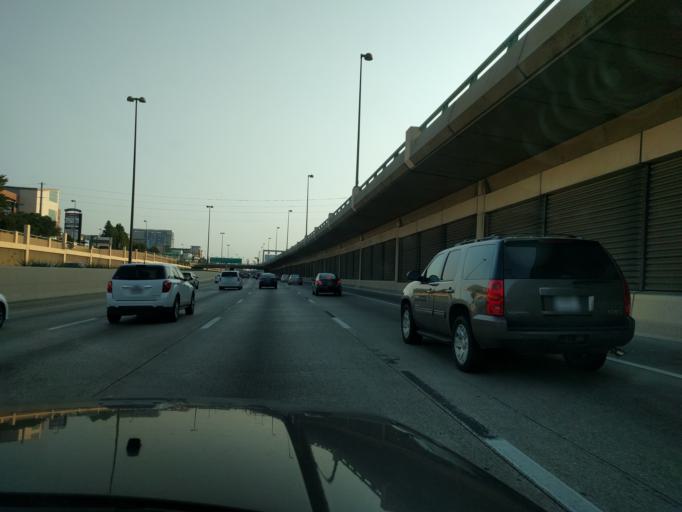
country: US
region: Texas
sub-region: Dallas County
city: Highland Park
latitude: 32.8192
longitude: -96.7873
